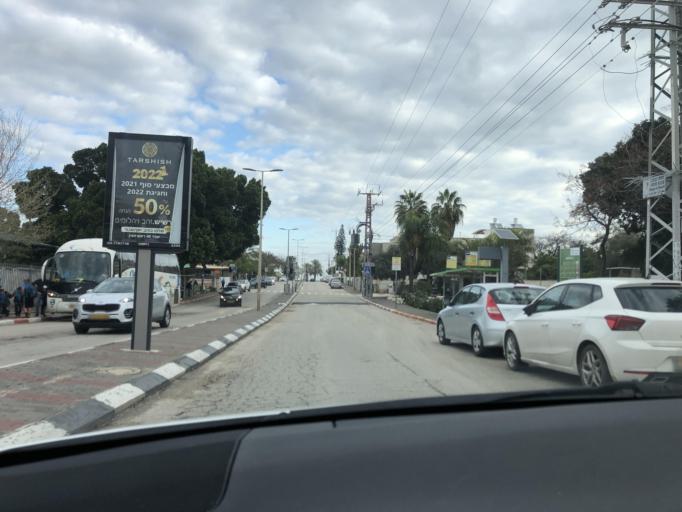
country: IL
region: Central District
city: Rosh Ha'Ayin
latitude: 32.0900
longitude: 34.9539
